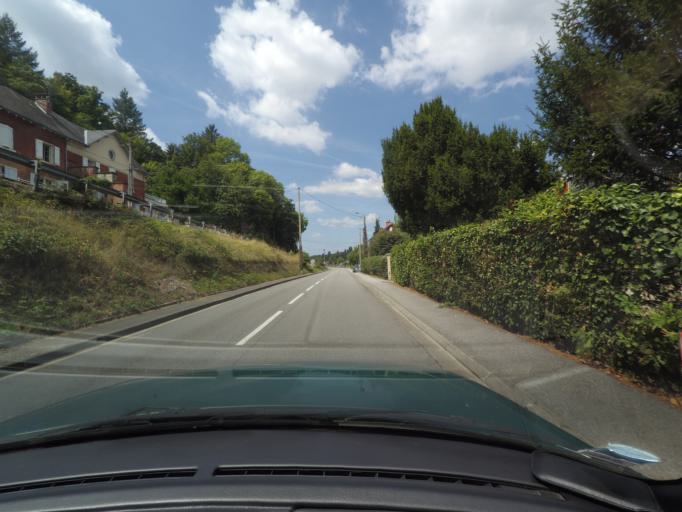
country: FR
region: Limousin
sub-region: Departement de la Haute-Vienne
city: Isle
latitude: 45.7774
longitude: 1.2067
